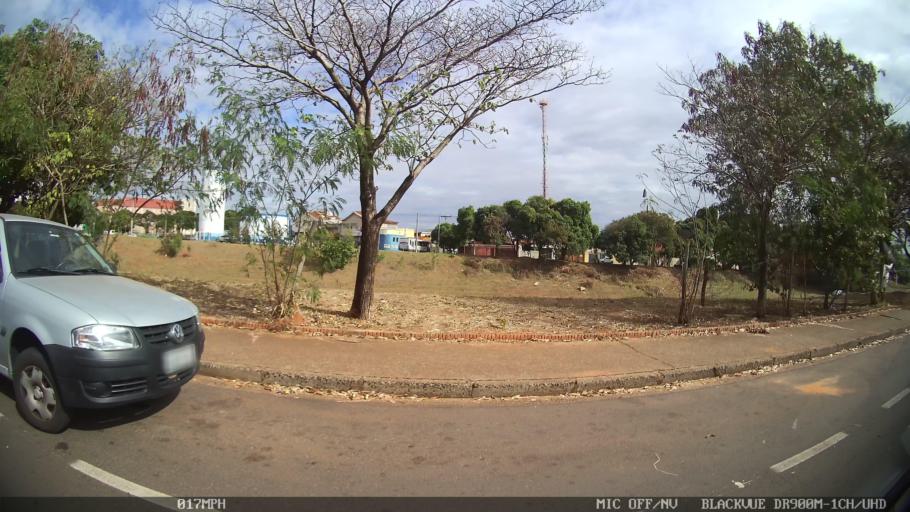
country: BR
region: Sao Paulo
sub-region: Sao Jose Do Rio Preto
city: Sao Jose do Rio Preto
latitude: -20.8170
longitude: -49.3568
